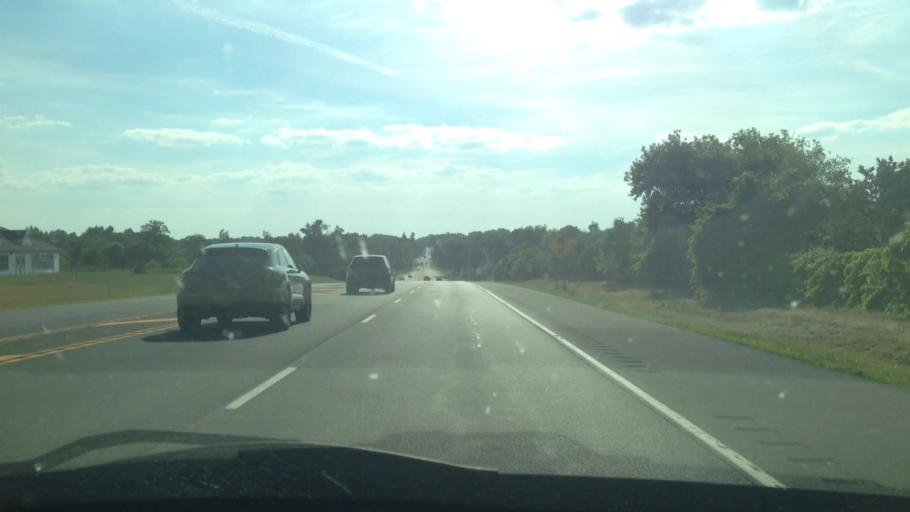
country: US
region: New York
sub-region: Onondaga County
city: Camillus
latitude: 43.0371
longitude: -76.3316
